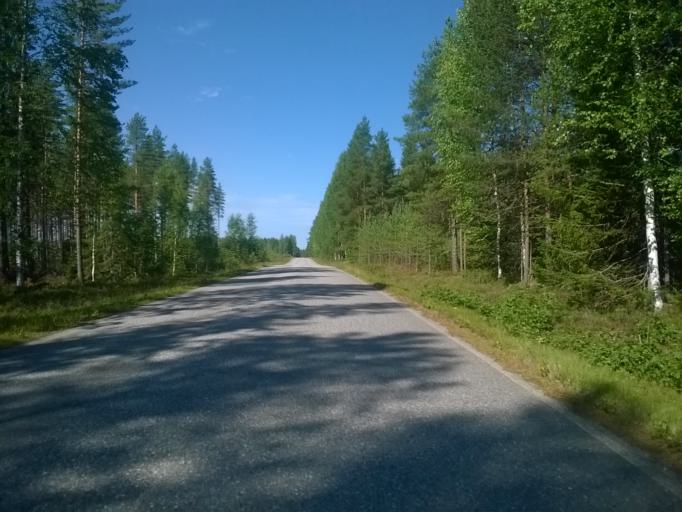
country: FI
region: Kainuu
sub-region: Kehys-Kainuu
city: Kuhmo
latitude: 64.1335
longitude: 29.4364
